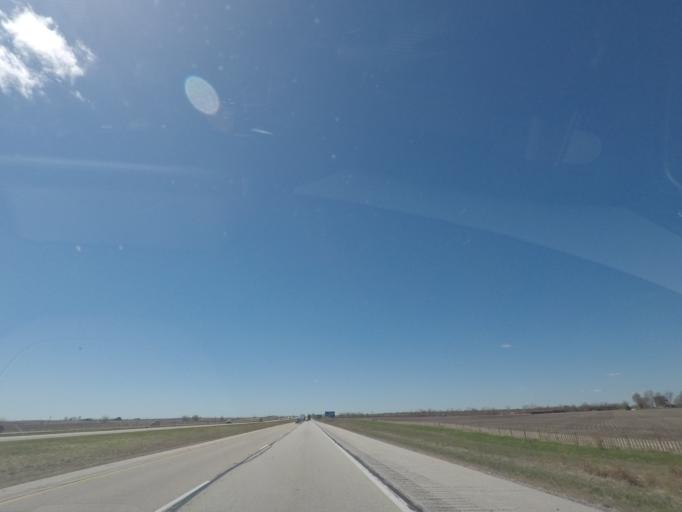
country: US
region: Illinois
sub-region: McLean County
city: Normal
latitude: 40.5522
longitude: -88.9185
